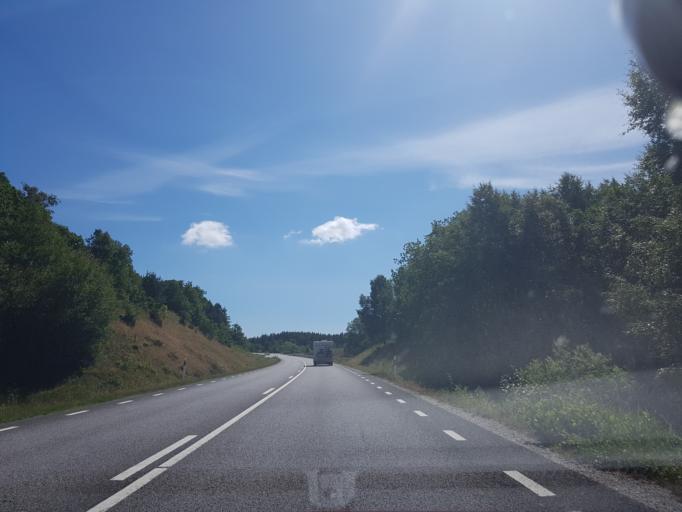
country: SE
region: Vaestra Goetaland
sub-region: Lysekils Kommun
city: Lysekil
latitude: 58.1549
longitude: 11.5253
